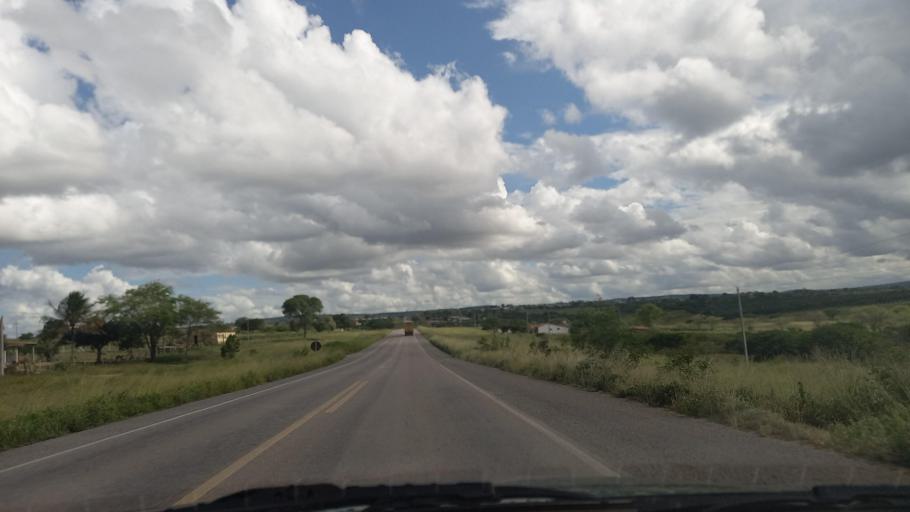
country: BR
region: Pernambuco
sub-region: Lajedo
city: Lajedo
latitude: -8.6355
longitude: -36.3069
